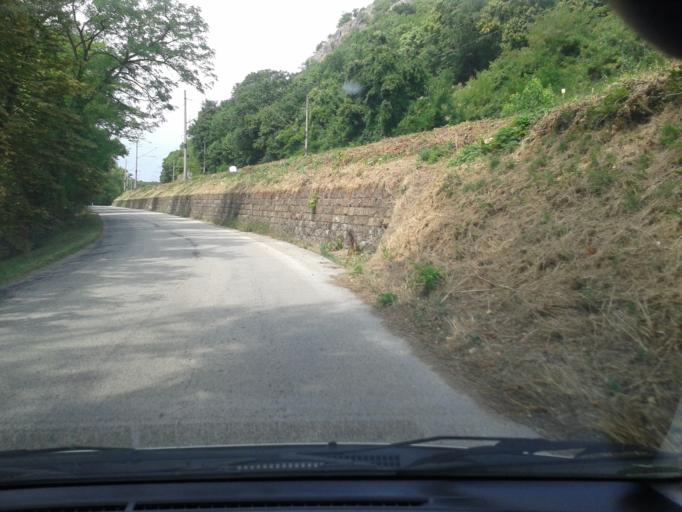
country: HU
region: Komarom-Esztergom
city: Esztergom
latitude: 47.8231
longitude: 18.7793
